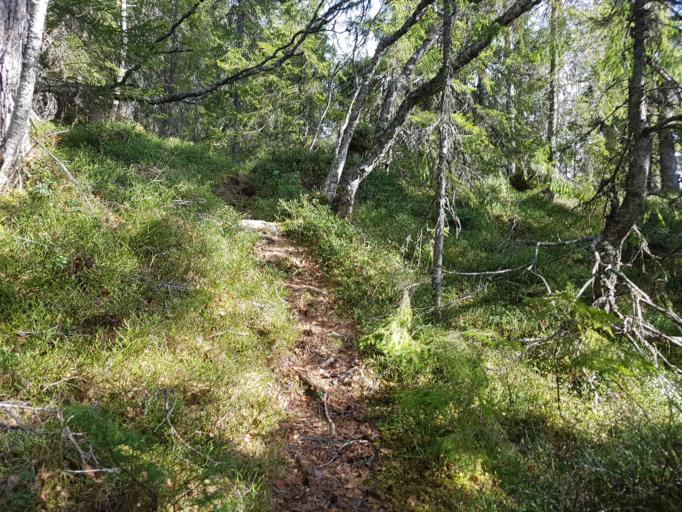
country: NO
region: Sor-Trondelag
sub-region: Trondheim
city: Trondheim
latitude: 63.4392
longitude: 10.2926
